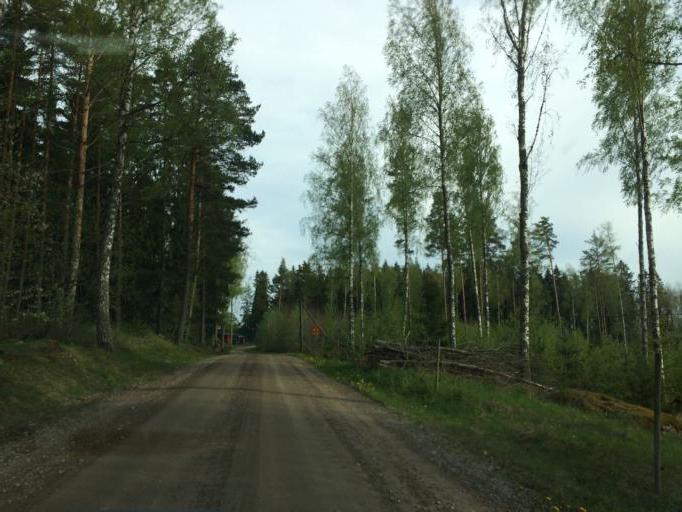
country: SE
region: Vaestmanland
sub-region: Hallstahammars Kommun
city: Hallstahammar
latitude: 59.6031
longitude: 16.0976
